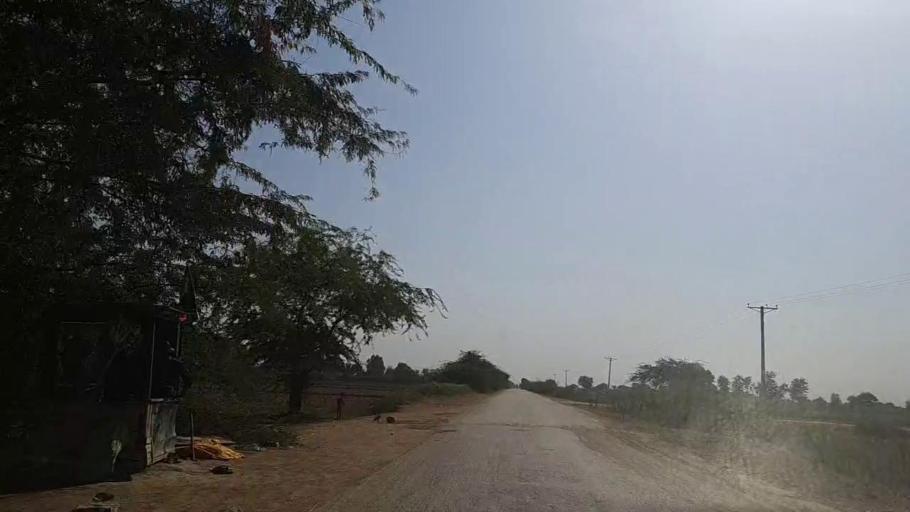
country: PK
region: Sindh
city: Mirpur Batoro
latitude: 24.6022
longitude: 68.2948
